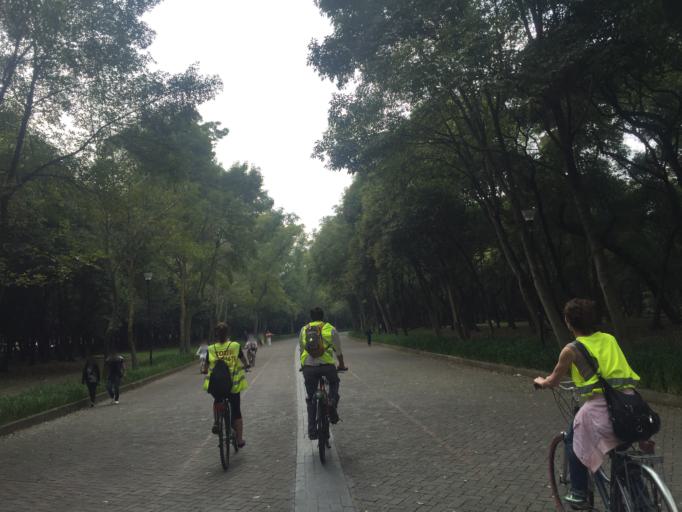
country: MX
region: Mexico City
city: Polanco
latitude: 19.4172
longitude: -99.1829
